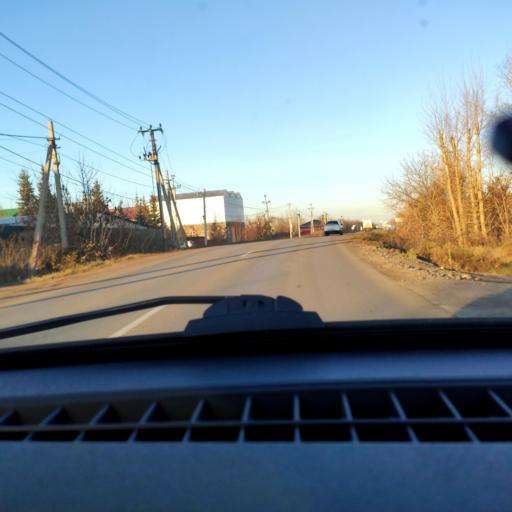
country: RU
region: Bashkortostan
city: Ufa
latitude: 54.6211
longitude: 55.9076
